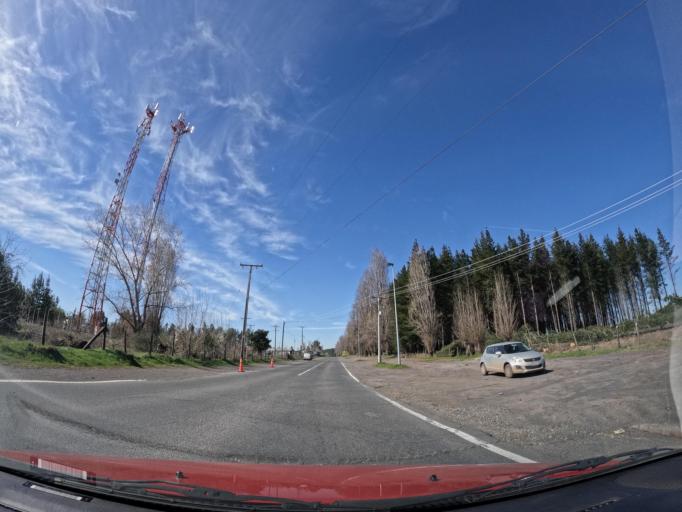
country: CL
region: Biobio
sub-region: Provincia de Biobio
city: Cabrero
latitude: -36.9397
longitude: -72.3479
